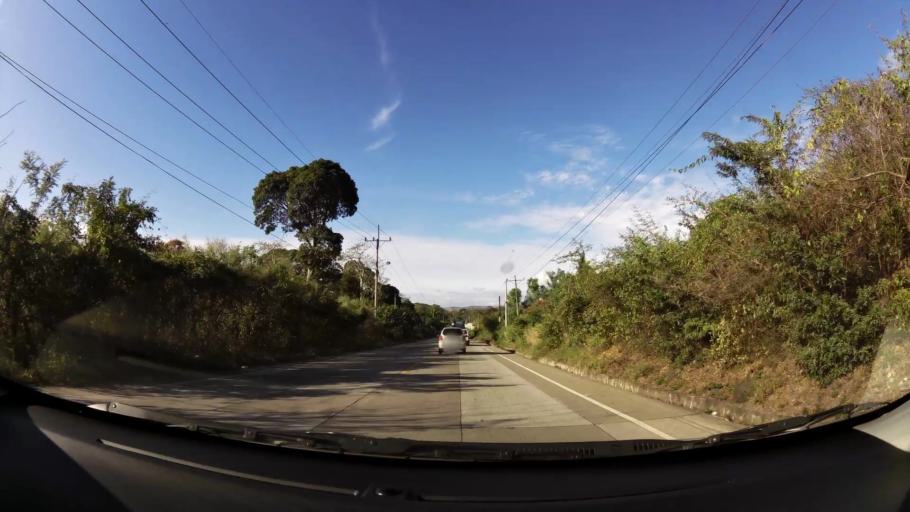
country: SV
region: Santa Ana
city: Metapan
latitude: 14.2753
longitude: -89.4607
